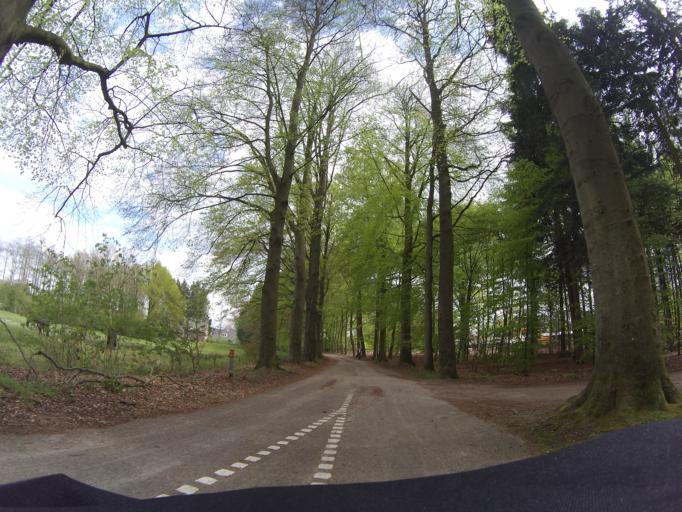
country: NL
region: Overijssel
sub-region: Gemeente Twenterand
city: Den Ham
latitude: 52.5115
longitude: 6.4156
